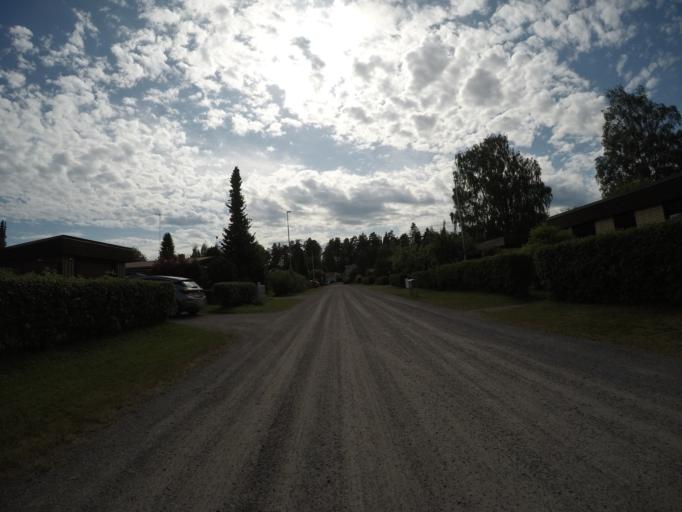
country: FI
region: Haeme
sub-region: Haemeenlinna
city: Haemeenlinna
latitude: 60.9843
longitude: 24.4026
